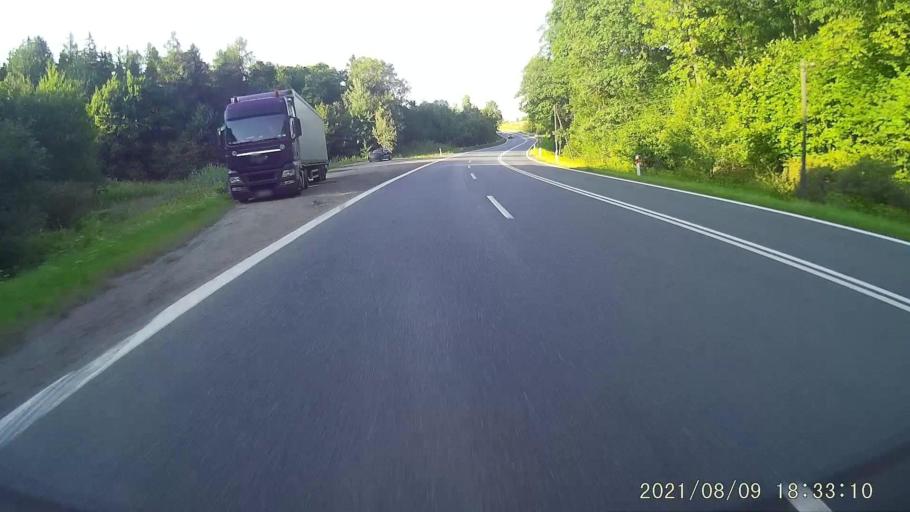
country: PL
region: Lower Silesian Voivodeship
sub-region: Powiat zabkowicki
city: Bardo
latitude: 50.4936
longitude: 16.7220
